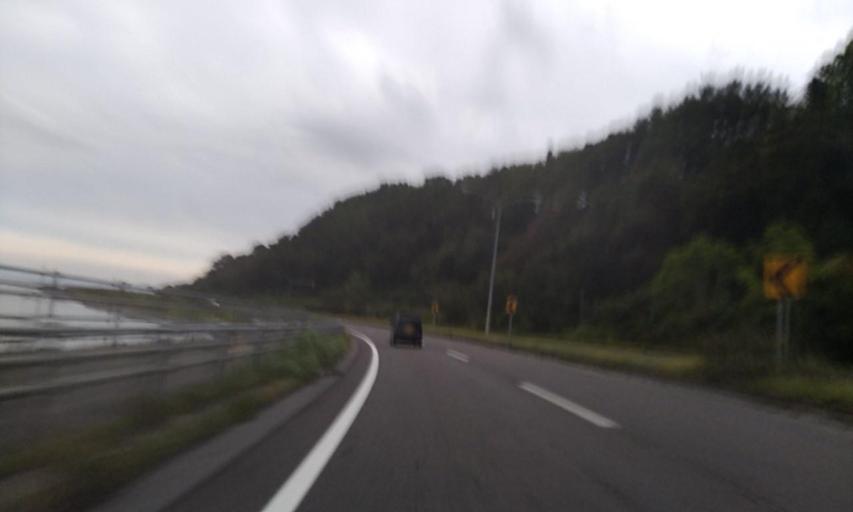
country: JP
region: Hokkaido
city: Abashiri
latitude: 43.9978
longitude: 144.2921
